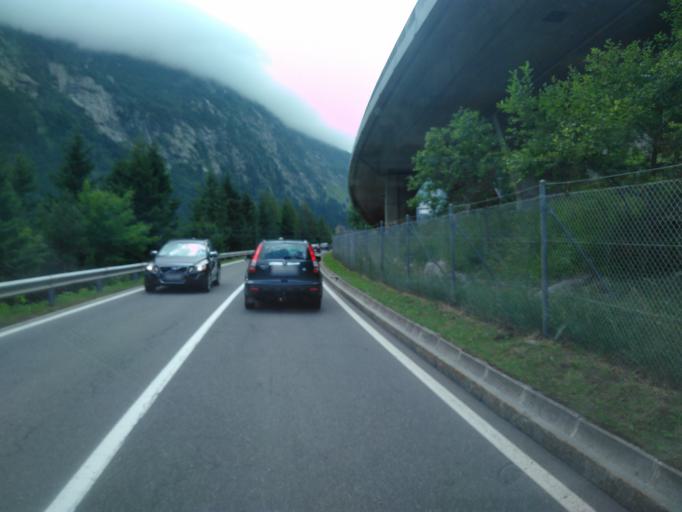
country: CH
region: Uri
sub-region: Uri
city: Andermatt
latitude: 46.6750
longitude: 8.5933
